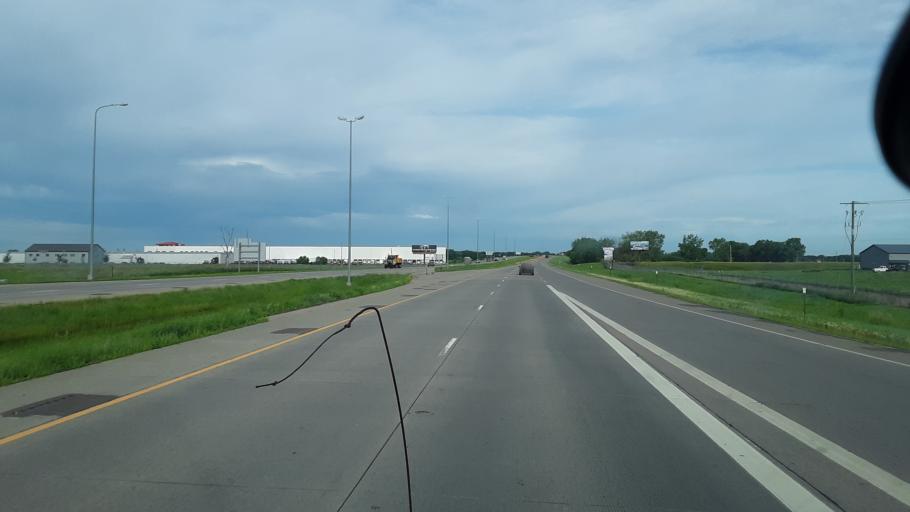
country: US
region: South Dakota
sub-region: Minnehaha County
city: Sioux Falls
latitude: 43.6060
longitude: -96.7168
